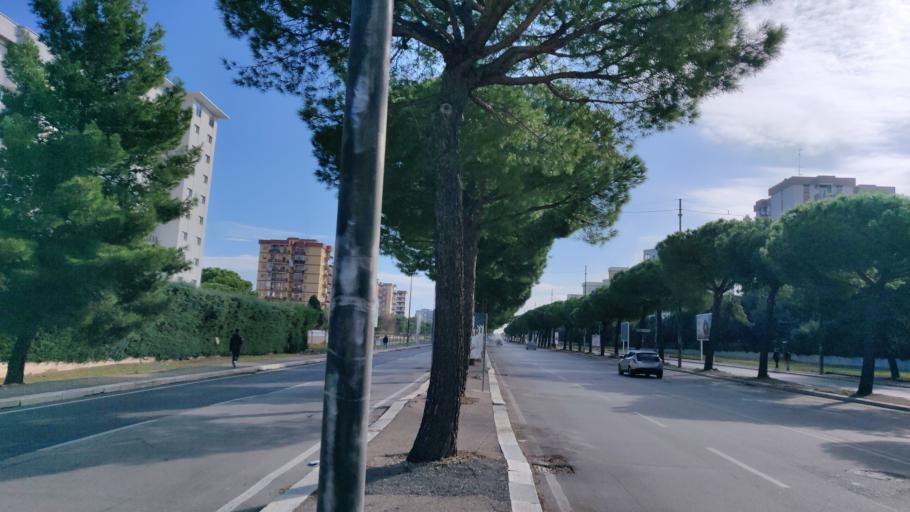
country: IT
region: Apulia
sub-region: Provincia di Bari
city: Triggiano
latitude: 41.1051
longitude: 16.9028
